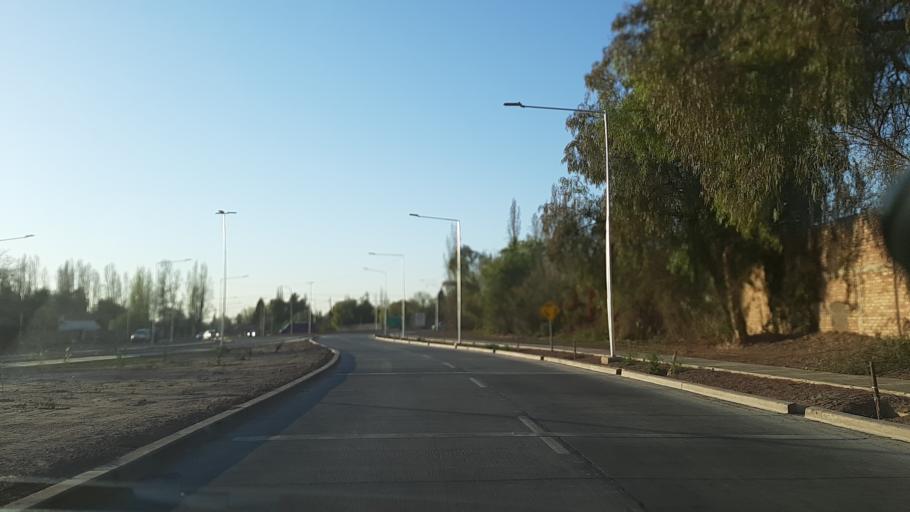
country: AR
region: Mendoza
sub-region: Departamento de Godoy Cruz
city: Godoy Cruz
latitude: -32.9632
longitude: -68.8630
